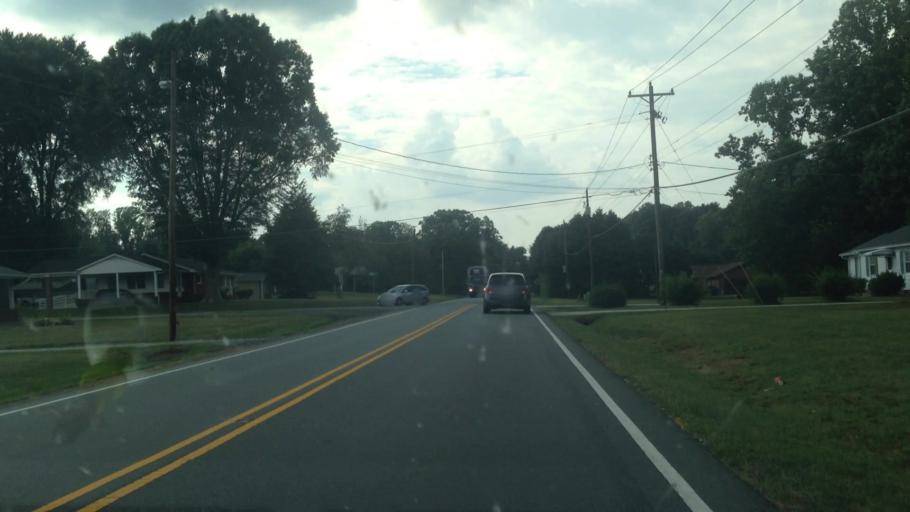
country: US
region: North Carolina
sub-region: Forsyth County
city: Walkertown
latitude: 36.1418
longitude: -80.1252
